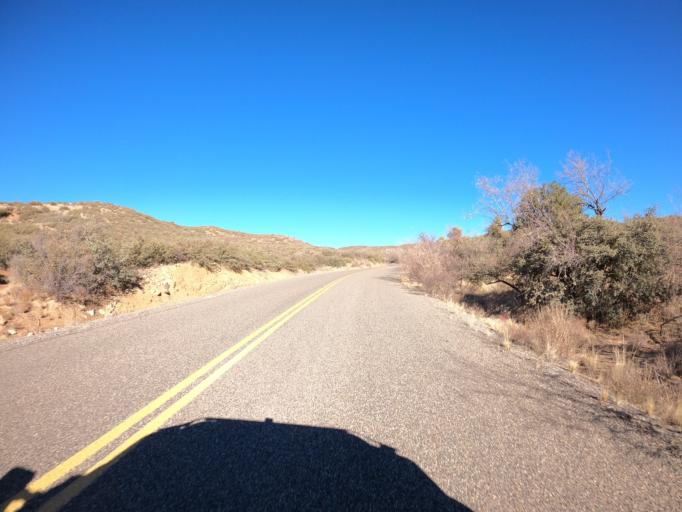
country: US
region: Arizona
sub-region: Yavapai County
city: Verde Village
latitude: 34.5563
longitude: -112.0735
